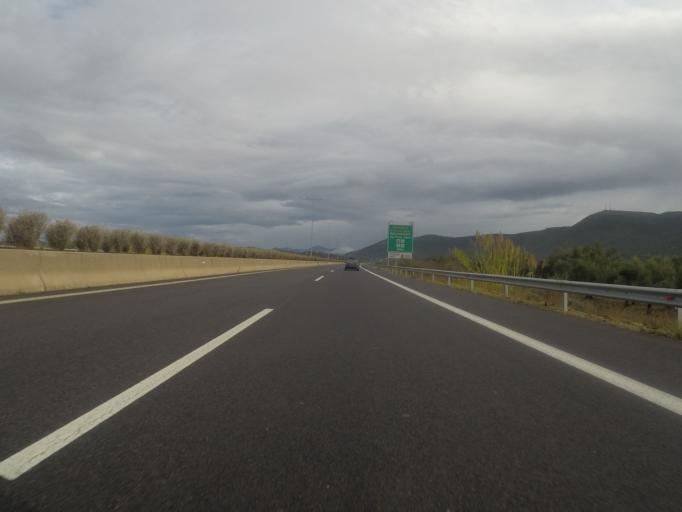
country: GR
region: Peloponnese
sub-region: Nomos Messinias
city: Arfara
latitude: 37.1710
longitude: 22.0134
